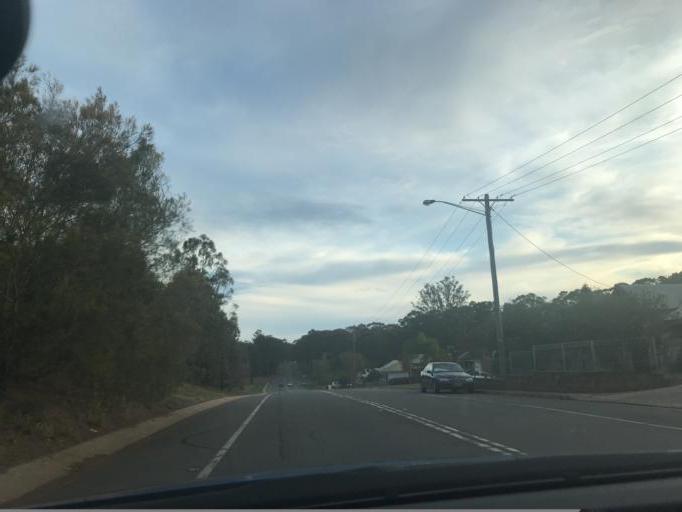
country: AU
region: New South Wales
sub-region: Cessnock
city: Cessnock
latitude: -32.8645
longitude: 151.3163
